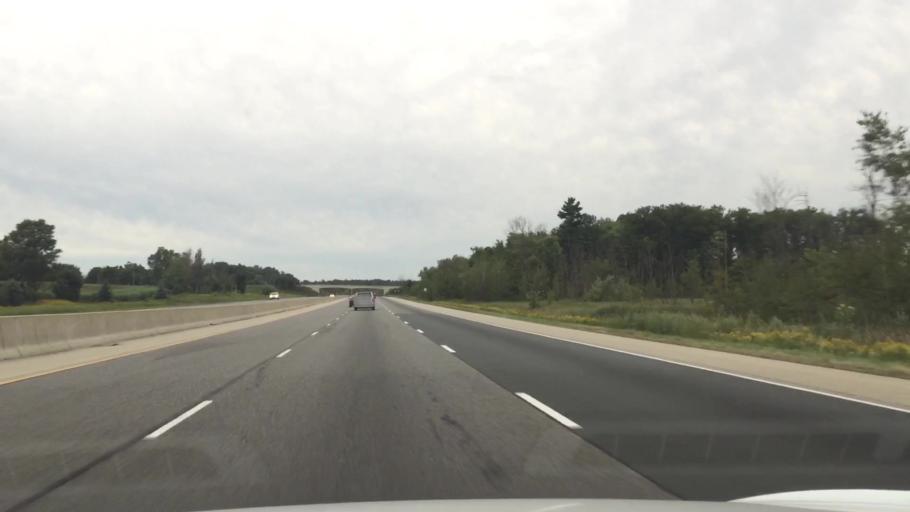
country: CA
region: Ontario
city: Kitchener
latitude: 43.2640
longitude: -80.5578
